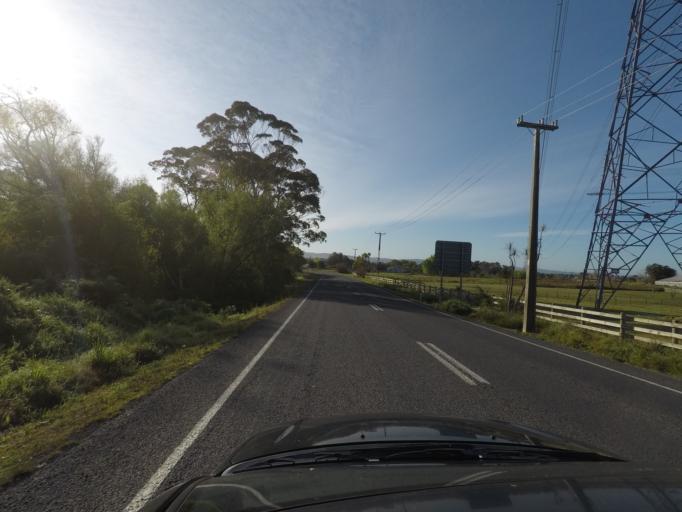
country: NZ
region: Auckland
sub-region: Auckland
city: Takanini
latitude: -37.0162
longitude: 174.9218
